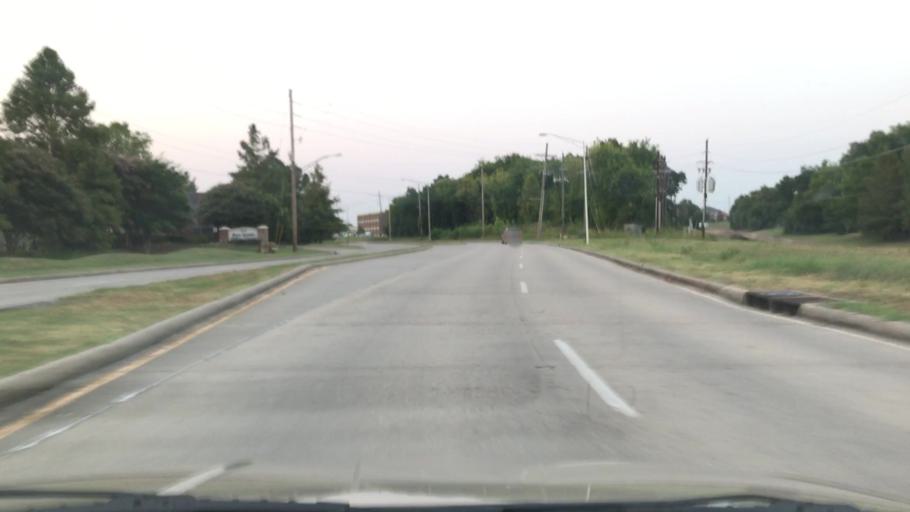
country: US
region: Louisiana
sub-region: Bossier Parish
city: Bossier City
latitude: 32.4373
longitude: -93.7285
